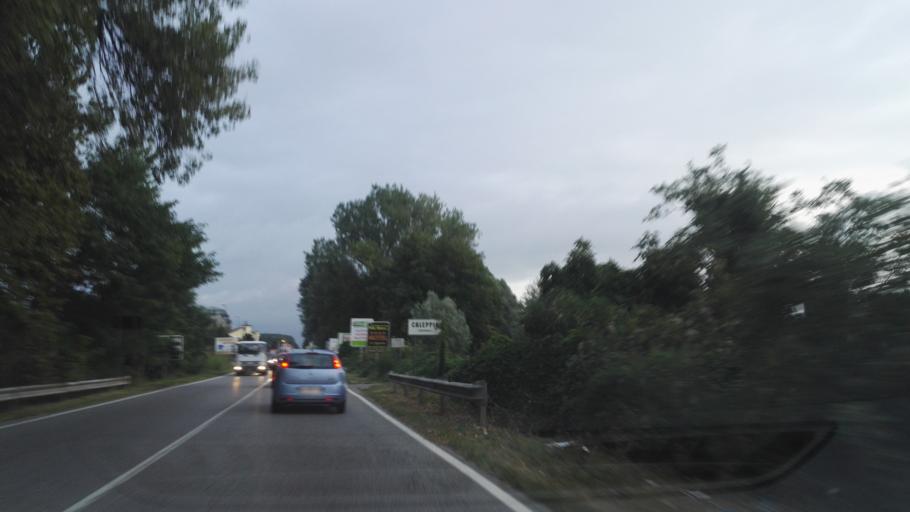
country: IT
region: Lombardy
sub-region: Citta metropolitana di Milano
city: Caleppio
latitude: 45.4304
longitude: 9.3764
